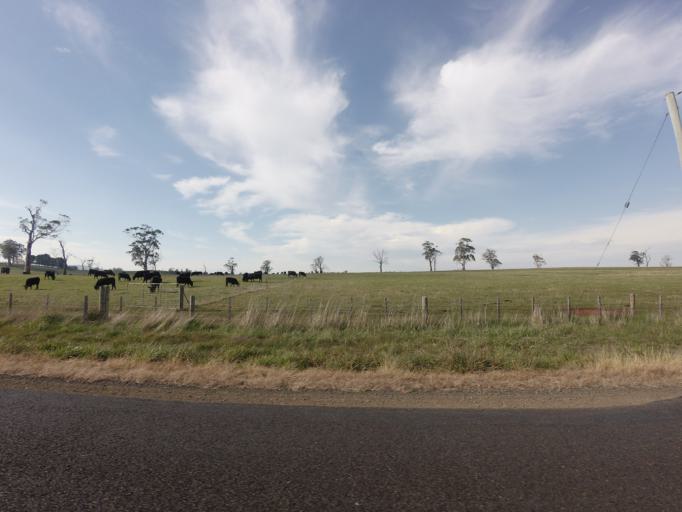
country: AU
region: Tasmania
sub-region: Northern Midlands
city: Longford
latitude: -41.5428
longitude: 146.9917
